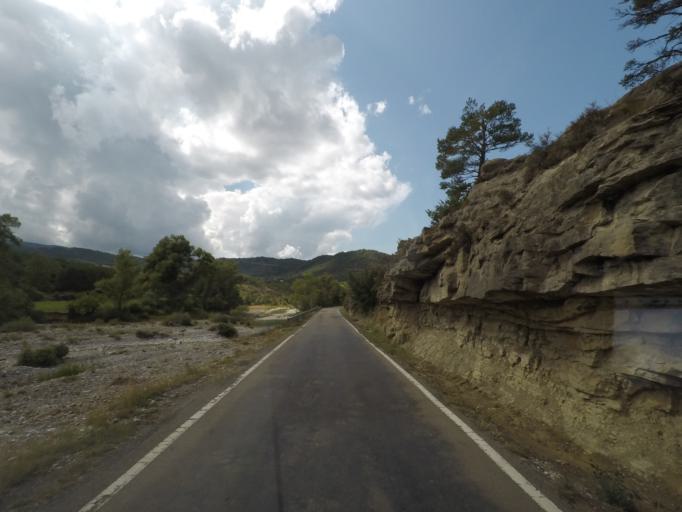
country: ES
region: Aragon
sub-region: Provincia de Huesca
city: Yebra de Basa
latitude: 42.3912
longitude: -0.3156
